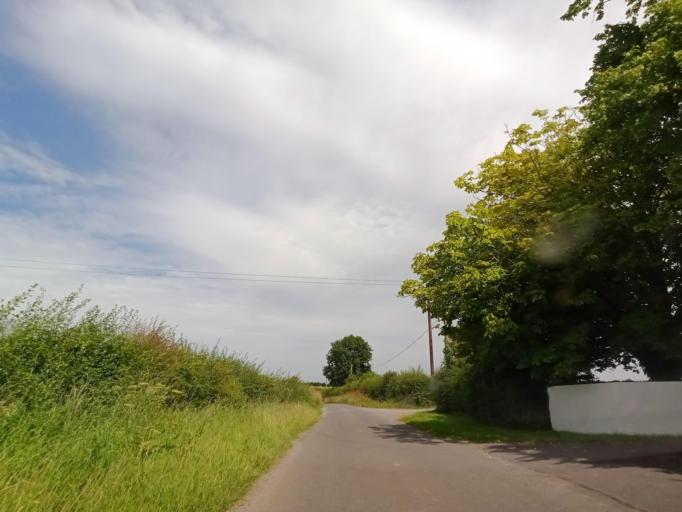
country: IE
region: Leinster
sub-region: Kilkenny
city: Thomastown
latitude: 52.5751
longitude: -7.1261
